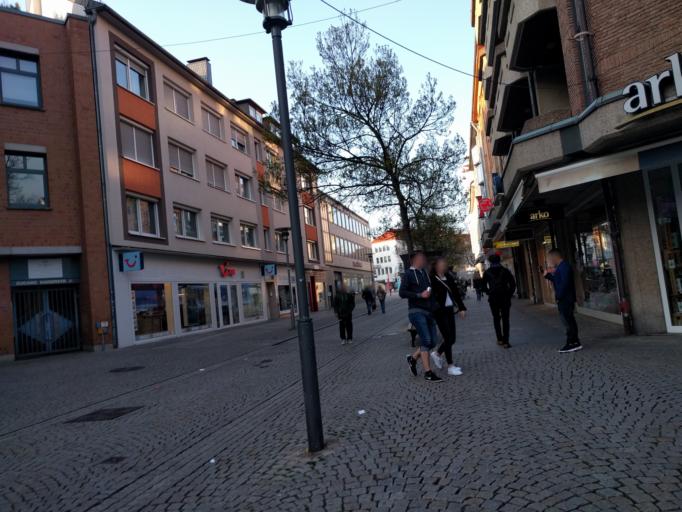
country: DE
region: Lower Saxony
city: Hildesheim
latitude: 52.1552
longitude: 9.9519
